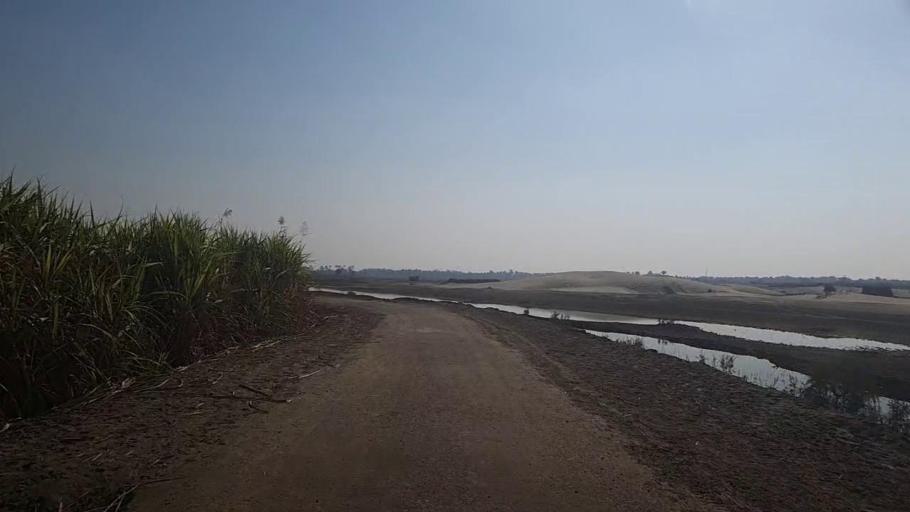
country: PK
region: Sindh
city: Kot Diji
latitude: 27.4348
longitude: 68.7278
